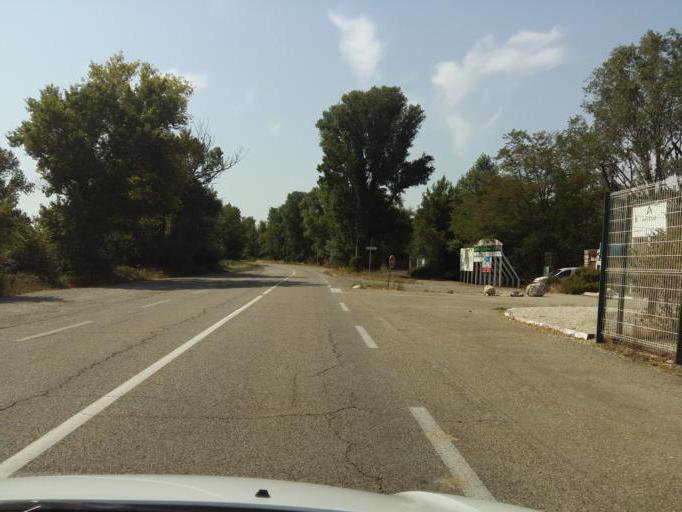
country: FR
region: Provence-Alpes-Cote d'Azur
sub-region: Departement du Vaucluse
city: Bollene
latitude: 44.3101
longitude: 4.7352
